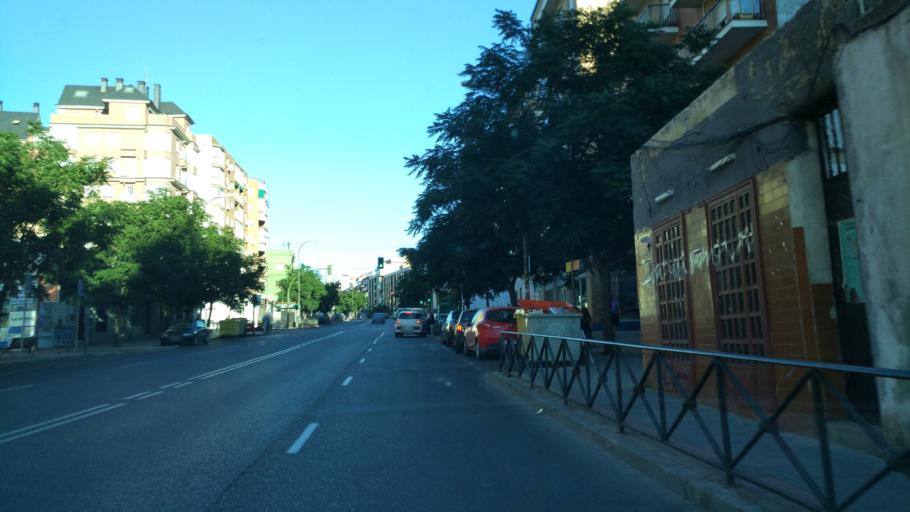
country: ES
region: Madrid
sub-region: Provincia de Madrid
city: Tetuan de las Victorias
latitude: 40.4621
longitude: -3.7014
